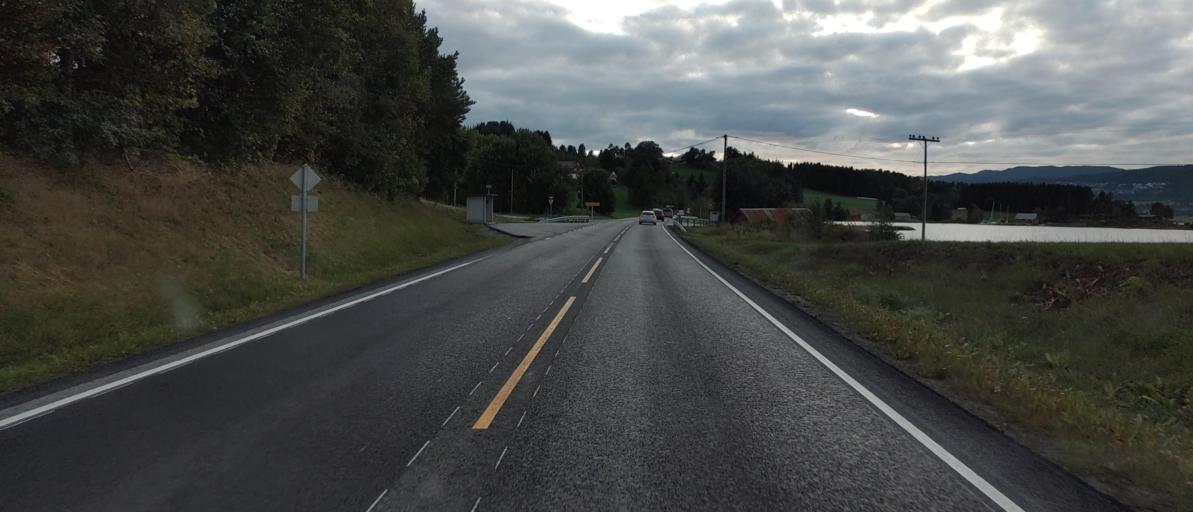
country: NO
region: More og Romsdal
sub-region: Molde
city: Hjelset
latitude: 62.7320
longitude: 7.3420
